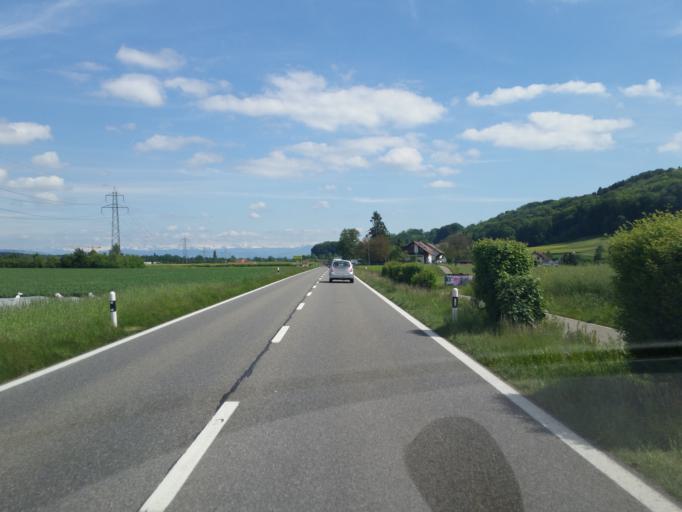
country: CH
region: Aargau
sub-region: Bezirk Bremgarten
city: Wohlen
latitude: 47.3370
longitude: 8.2767
